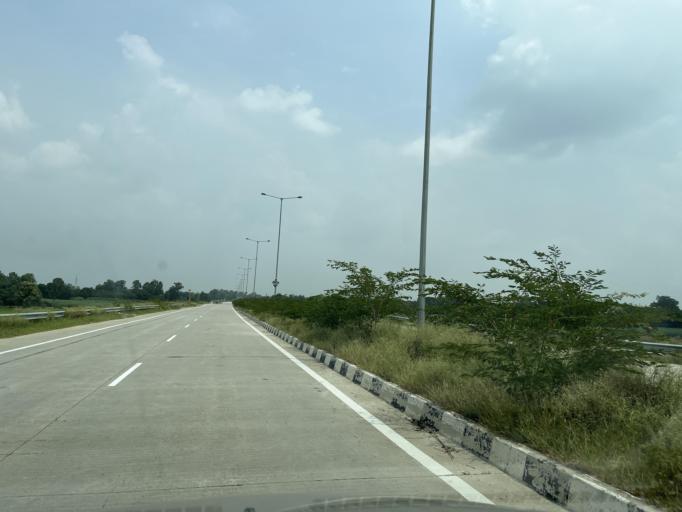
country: IN
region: Uttar Pradesh
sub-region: Bijnor
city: Nagina
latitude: 29.4252
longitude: 78.4331
